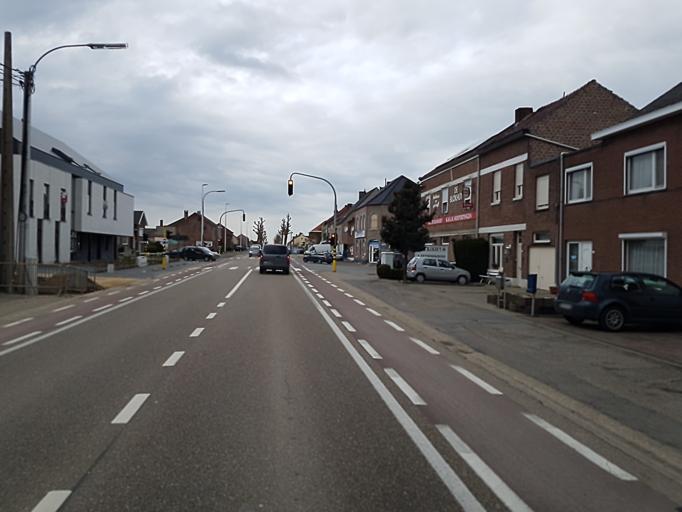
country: BE
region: Flanders
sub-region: Provincie Limburg
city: Heers
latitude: 50.8066
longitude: 5.2874
